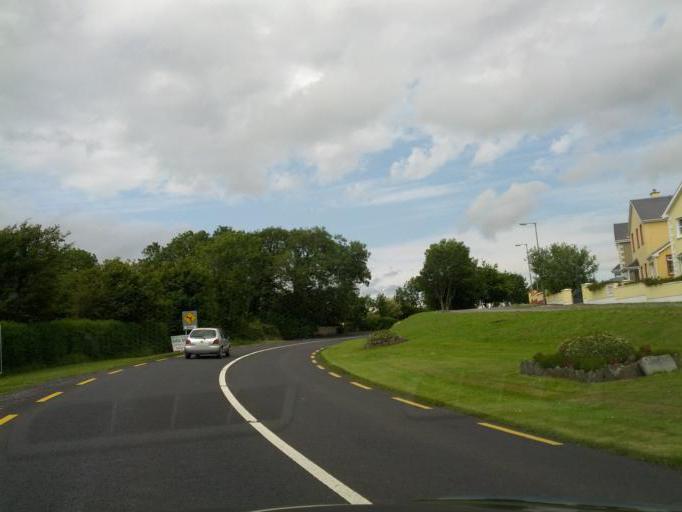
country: IE
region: Munster
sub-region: An Clar
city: Kilrush
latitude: 52.6425
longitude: -9.4924
